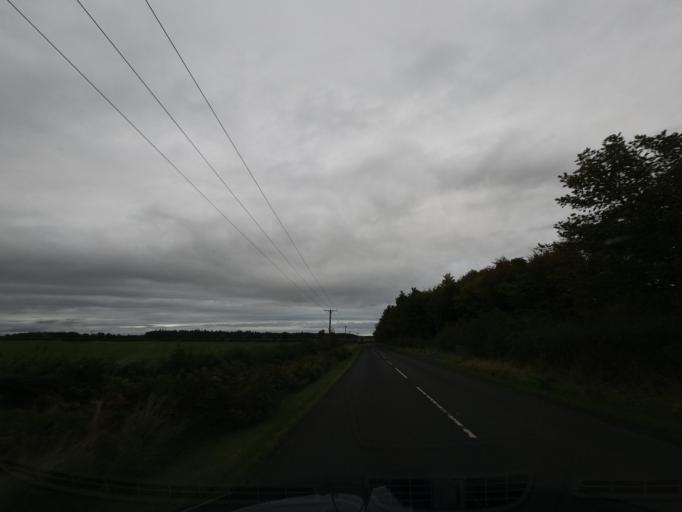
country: GB
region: England
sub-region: Northumberland
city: Ford
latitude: 55.6895
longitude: -2.0819
